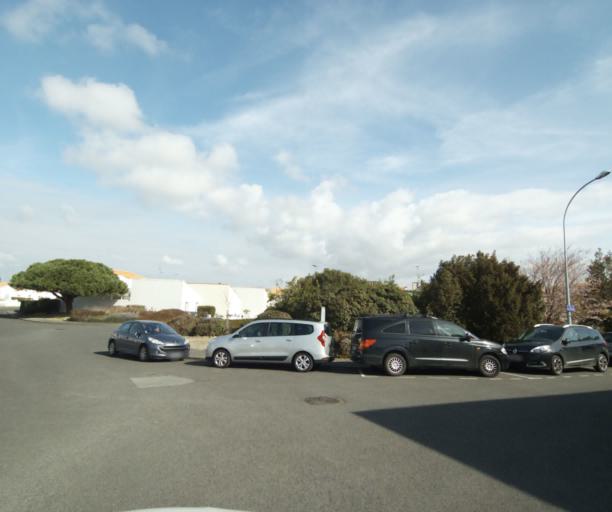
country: FR
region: Poitou-Charentes
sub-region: Departement de la Charente-Maritime
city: La Rochelle
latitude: 46.1707
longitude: -1.1702
